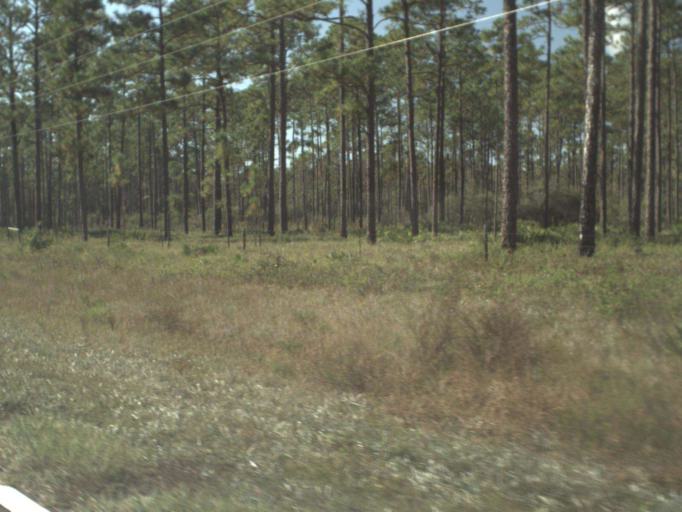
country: US
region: Florida
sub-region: Liberty County
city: Bristol
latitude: 30.1923
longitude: -84.9241
